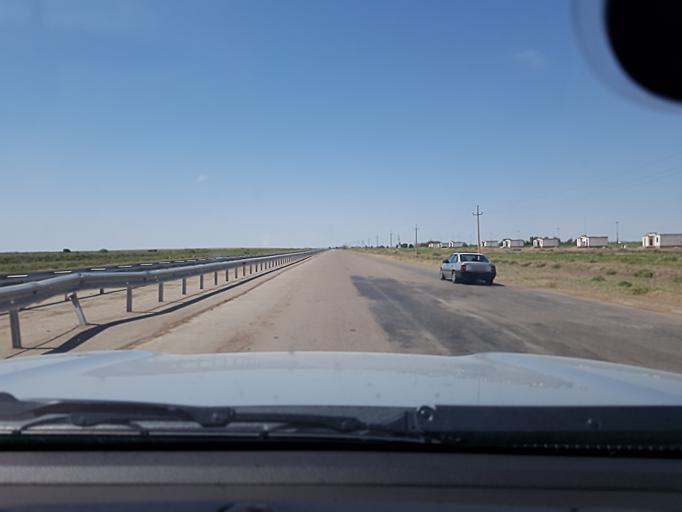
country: TM
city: Akdepe
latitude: 41.7404
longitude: 59.2366
